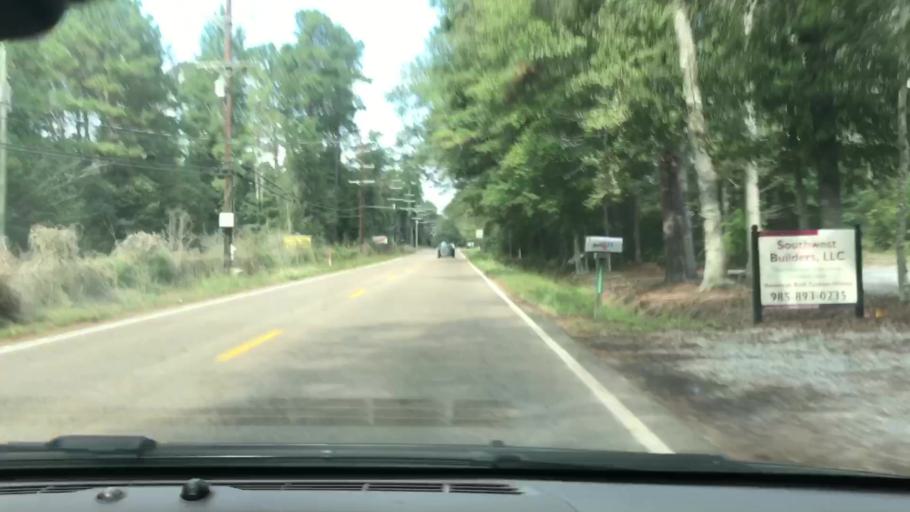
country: US
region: Louisiana
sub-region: Saint Tammany Parish
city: Abita Springs
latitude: 30.4668
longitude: -90.0407
